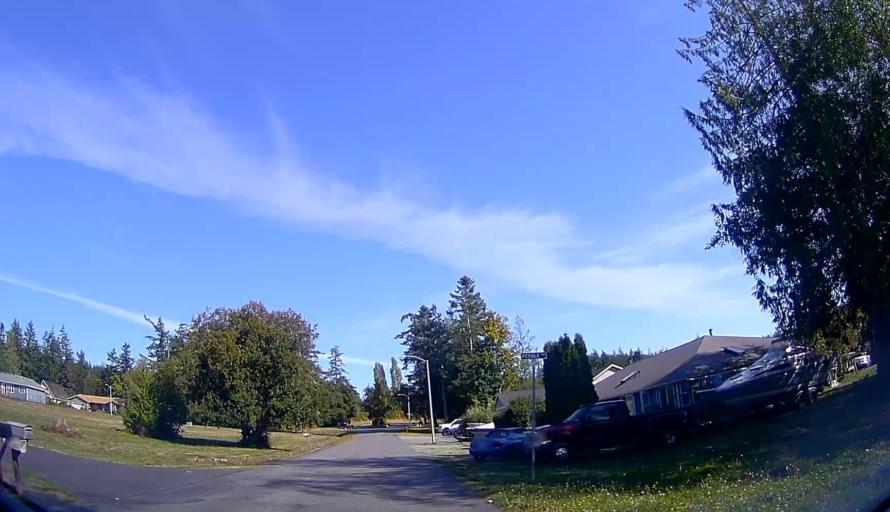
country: US
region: Washington
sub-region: Island County
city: Camano
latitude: 48.1824
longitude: -122.5294
